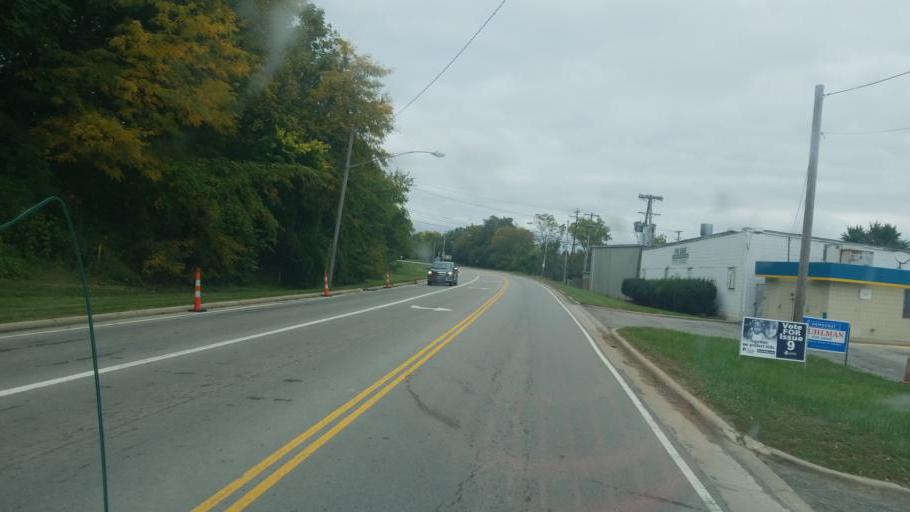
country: US
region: Ohio
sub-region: Lucas County
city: Waterville
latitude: 41.5009
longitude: -83.7197
